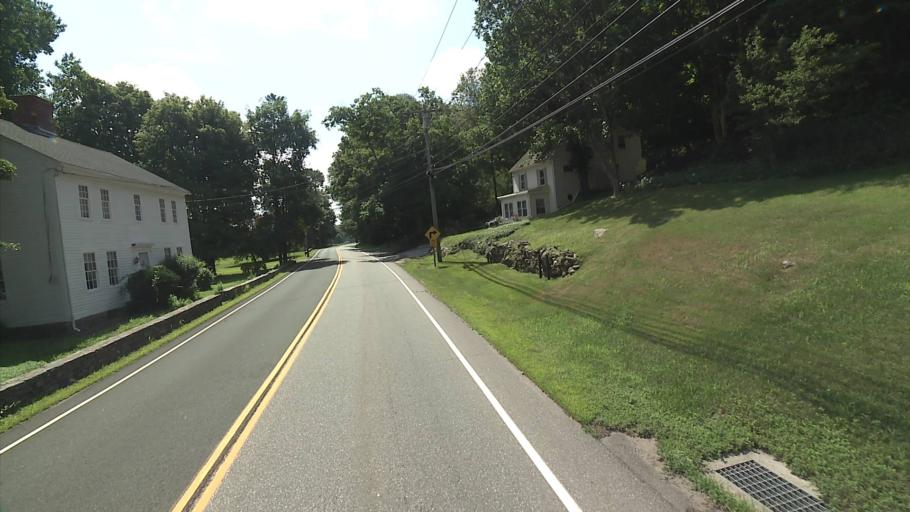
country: US
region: Connecticut
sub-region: Middlesex County
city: Essex Village
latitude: 41.3471
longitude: -72.4153
